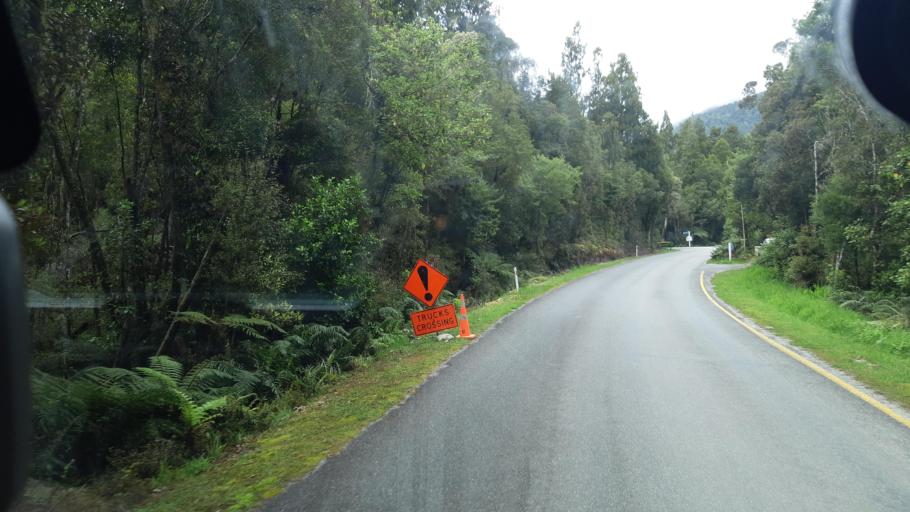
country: NZ
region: West Coast
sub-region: Westland District
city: Hokitika
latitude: -42.7996
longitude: 171.1507
